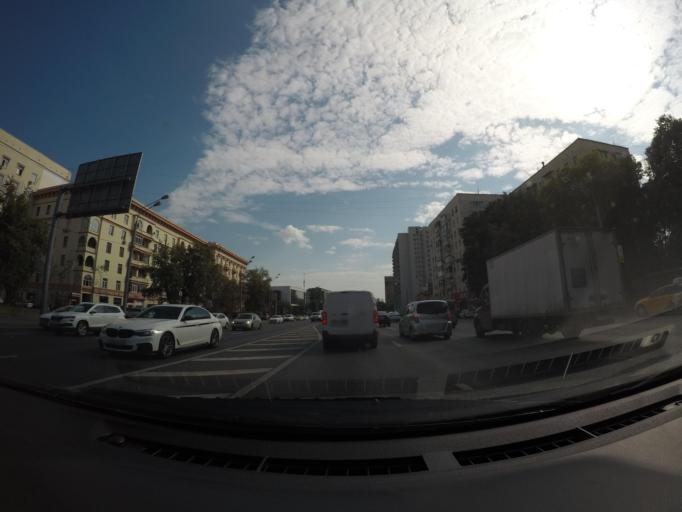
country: RU
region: Moscow
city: Mar'ina Roshcha
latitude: 55.8069
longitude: 37.5815
